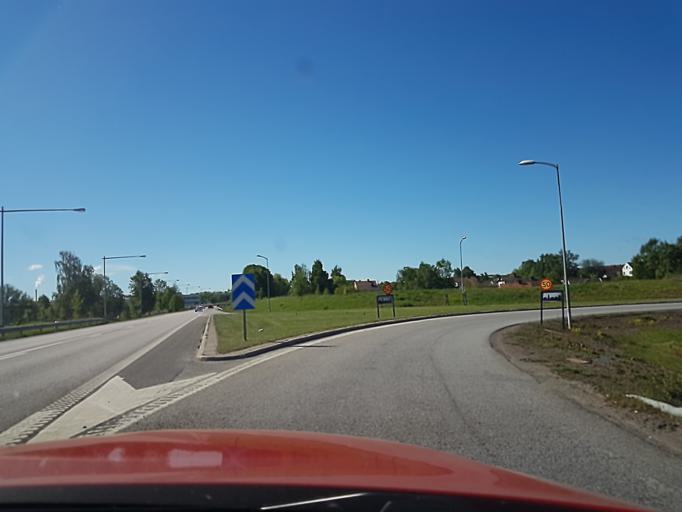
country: SE
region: Vaestra Goetaland
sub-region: Skovde Kommun
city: Skoevde
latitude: 58.3937
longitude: 13.8738
